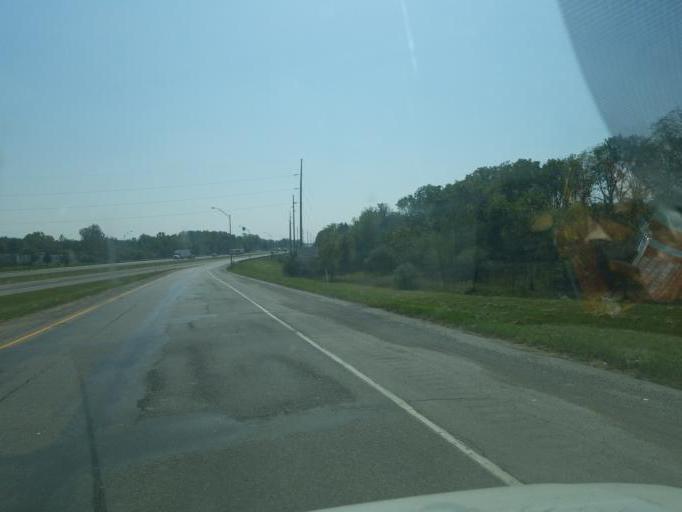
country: US
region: Indiana
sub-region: Steuben County
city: Angola
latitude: 41.6335
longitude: -85.0485
